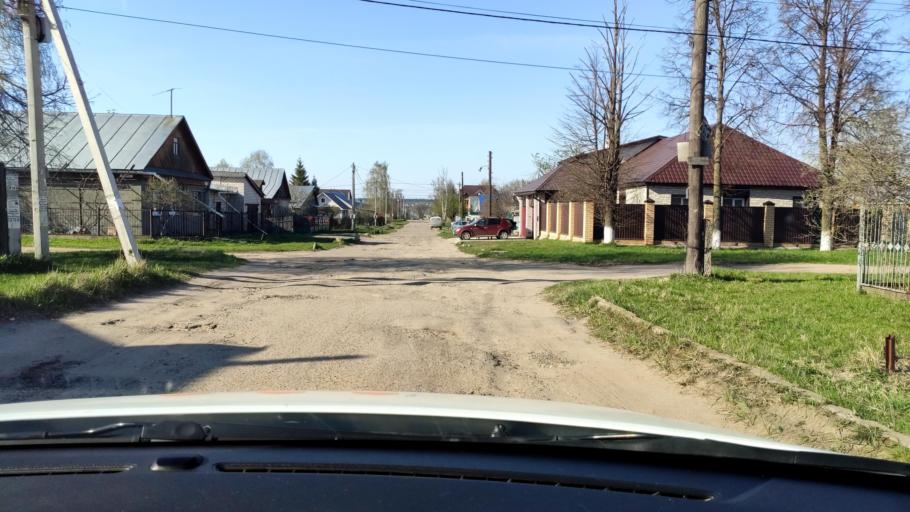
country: RU
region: Tatarstan
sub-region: Gorod Kazan'
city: Kazan
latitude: 55.8676
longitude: 49.0602
